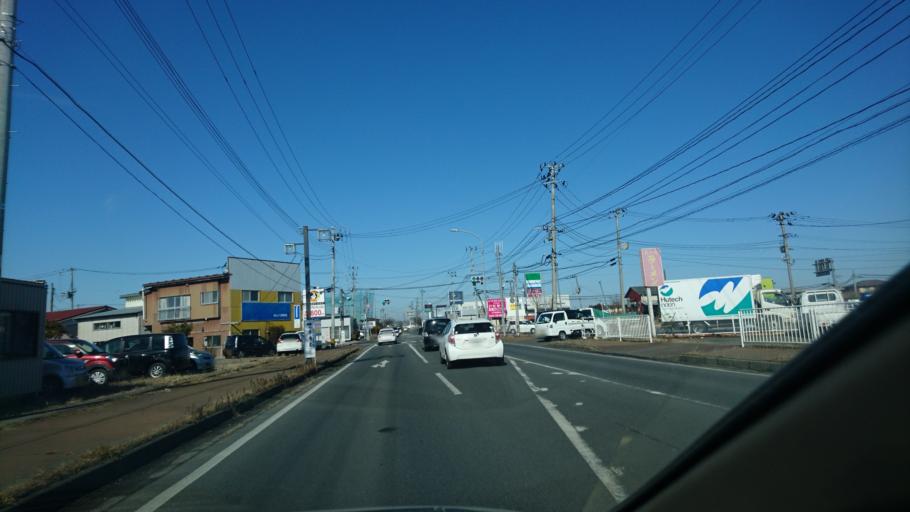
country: JP
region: Miyagi
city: Furukawa
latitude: 38.5945
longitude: 140.9765
